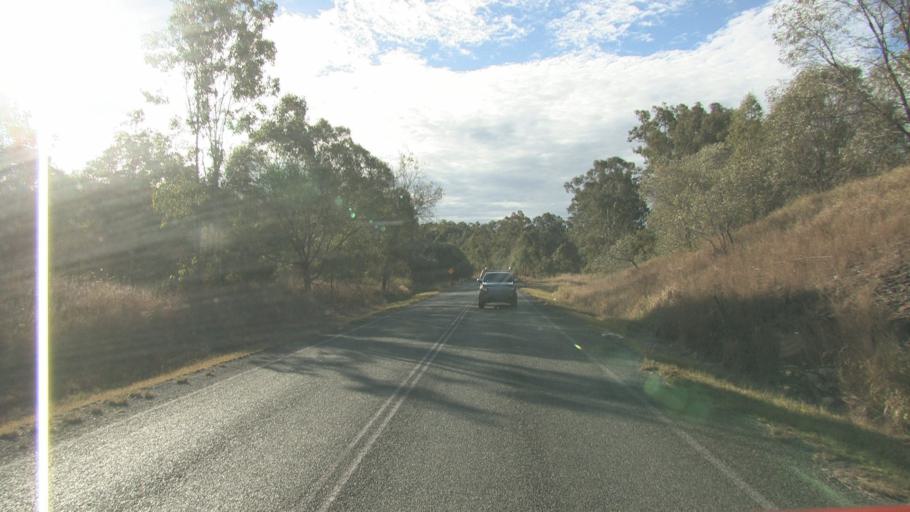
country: AU
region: Queensland
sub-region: Logan
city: Cedar Vale
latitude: -27.8964
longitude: 153.0882
